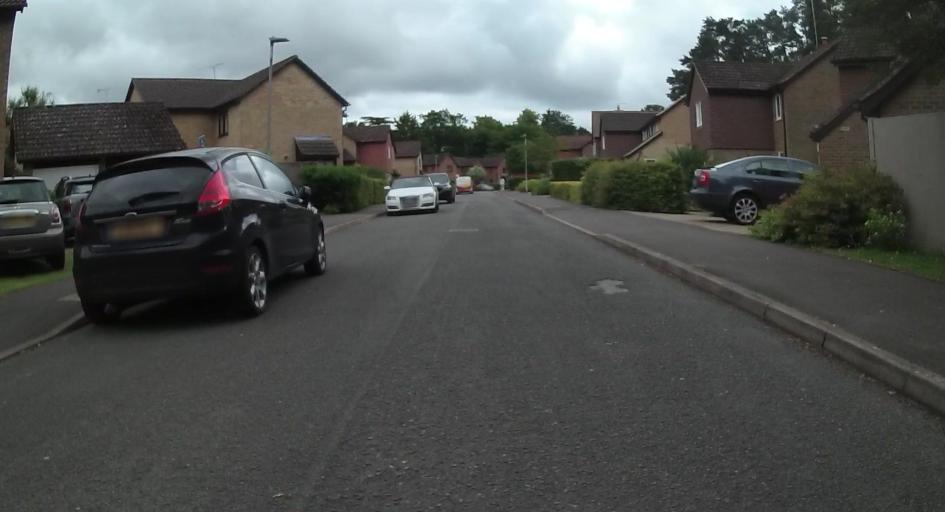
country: GB
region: England
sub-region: Bracknell Forest
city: Crowthorne
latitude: 51.3653
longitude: -0.7993
